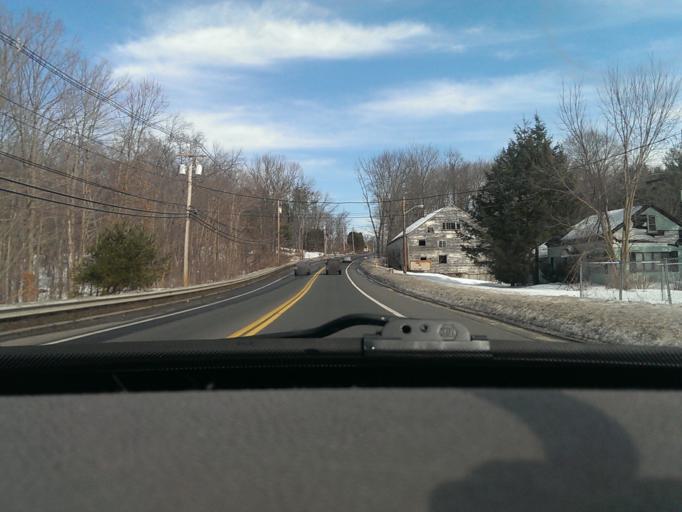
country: US
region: Massachusetts
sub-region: Hampden County
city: Three Rivers
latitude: 42.1531
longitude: -72.3764
